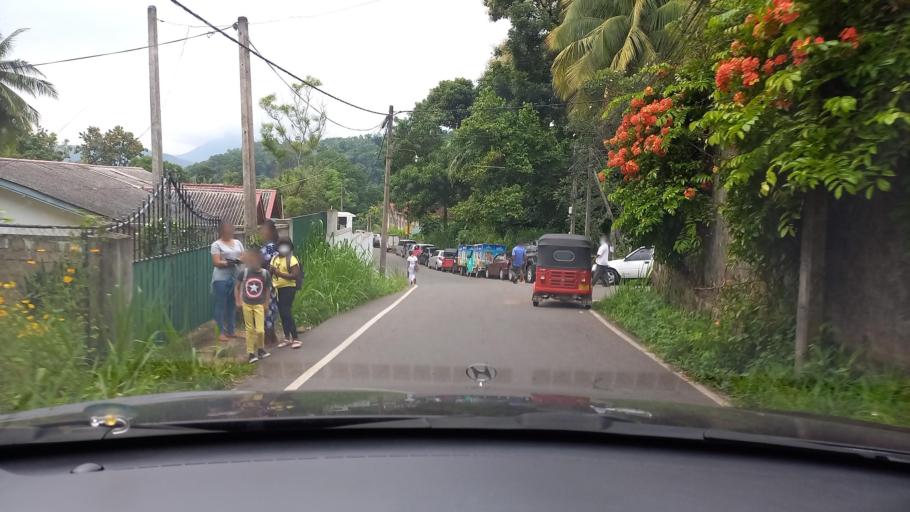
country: LK
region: Central
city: Kadugannawa
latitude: 7.2576
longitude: 80.3505
